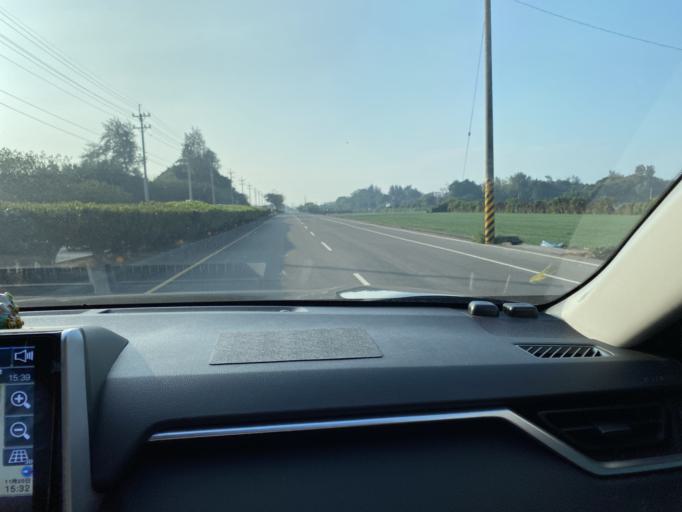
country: TW
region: Taiwan
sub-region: Changhua
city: Chang-hua
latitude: 23.9600
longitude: 120.3961
